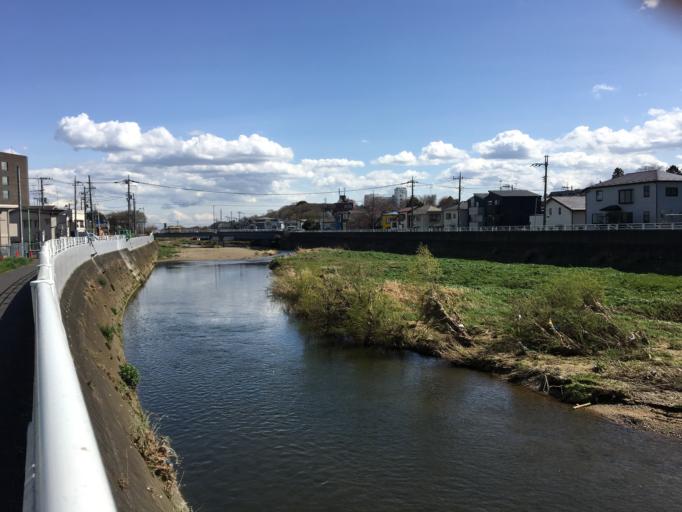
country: JP
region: Saitama
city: Shiki
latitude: 35.8371
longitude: 139.5783
